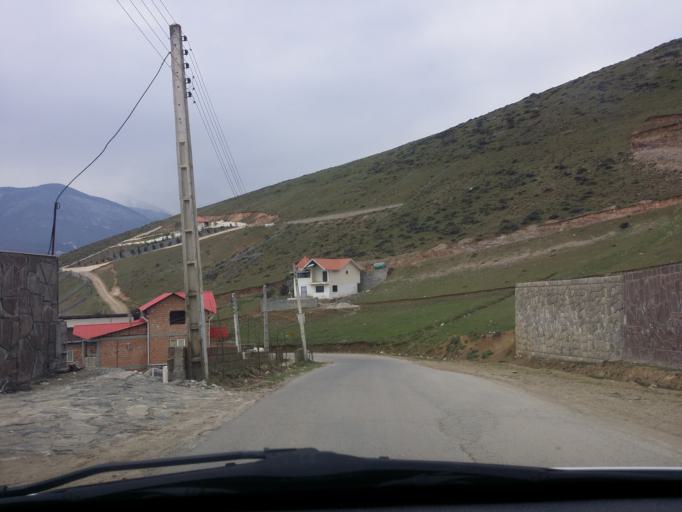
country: IR
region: Mazandaran
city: `Abbasabad
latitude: 36.5296
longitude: 51.1600
